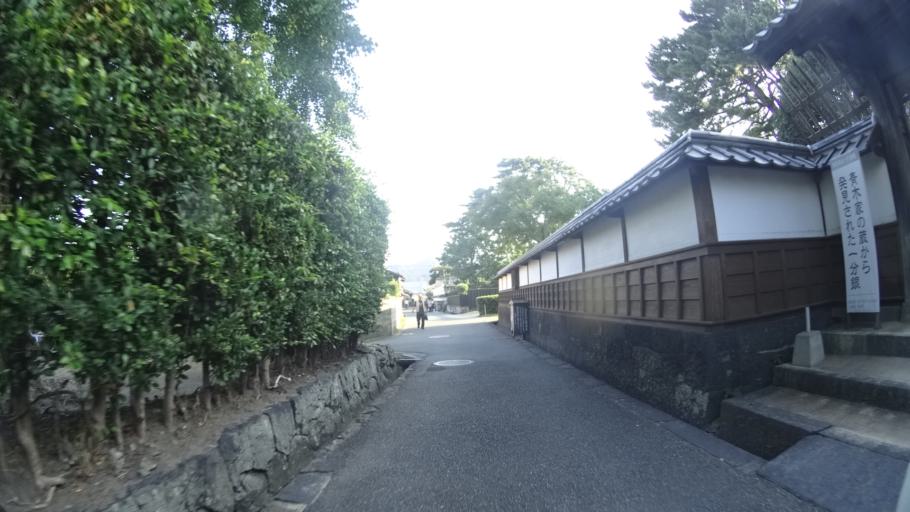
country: JP
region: Yamaguchi
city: Hagi
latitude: 34.4118
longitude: 131.3947
